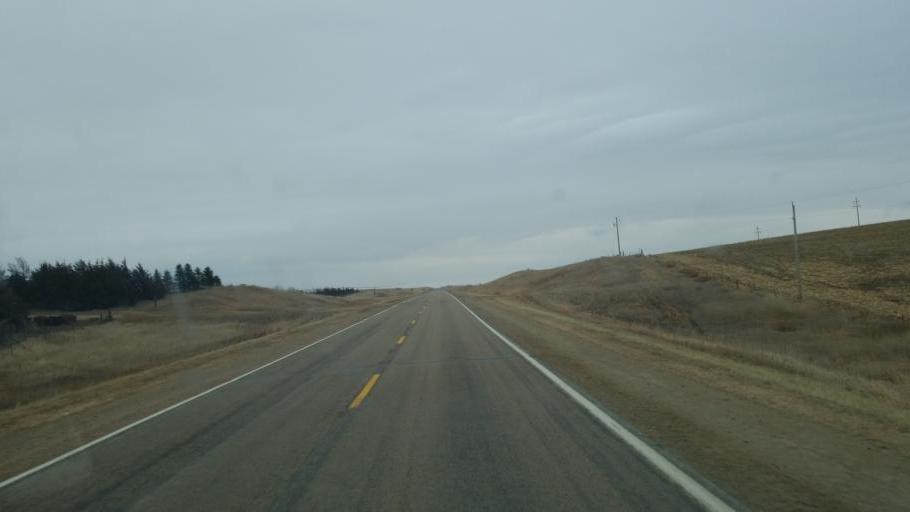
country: US
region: Nebraska
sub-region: Knox County
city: Bloomfield
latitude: 42.5979
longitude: -97.5586
